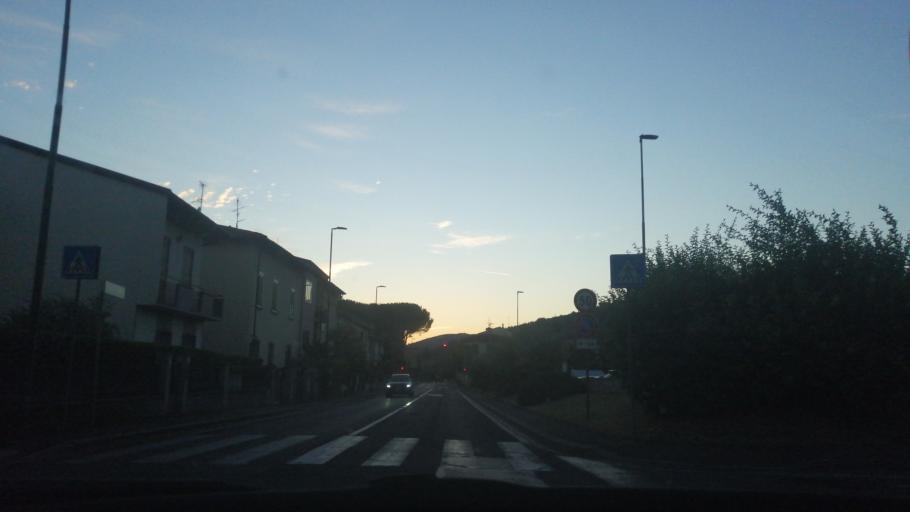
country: IT
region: Tuscany
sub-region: Province of Florence
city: Sesto Fiorentino
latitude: 43.8396
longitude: 11.2018
